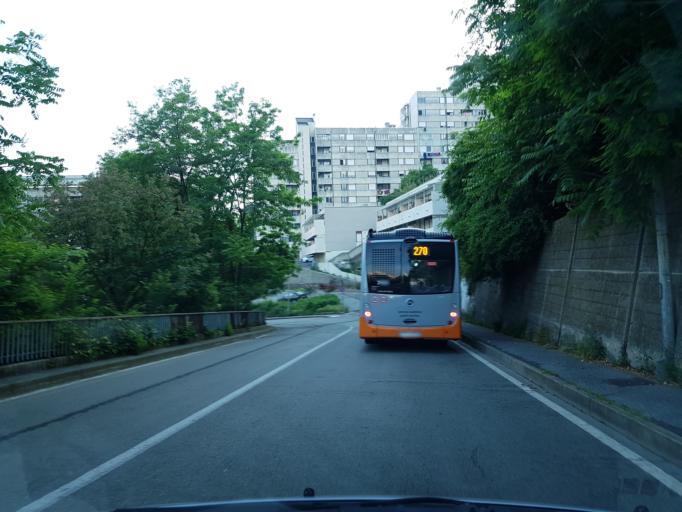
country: IT
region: Liguria
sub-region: Provincia di Genova
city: Genoa
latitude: 44.4474
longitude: 8.9032
